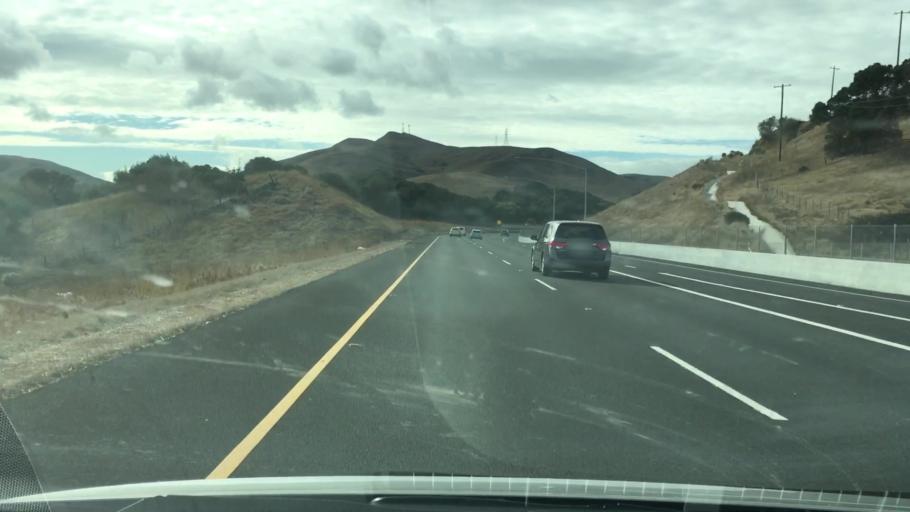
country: US
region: California
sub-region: Solano County
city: Green Valley
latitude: 38.2093
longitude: -122.1507
